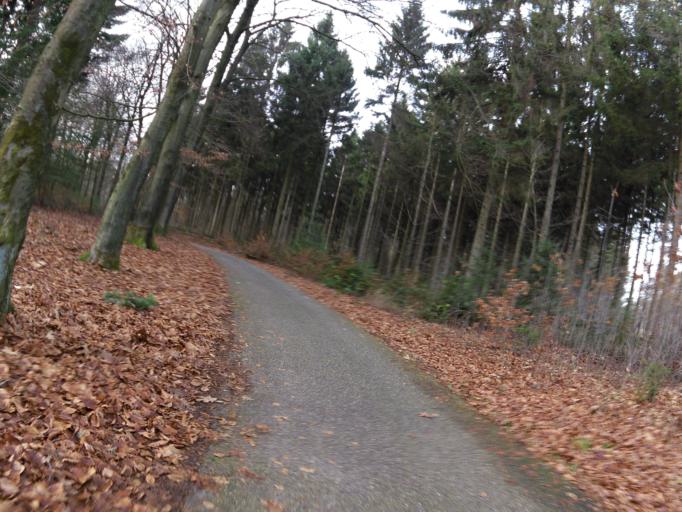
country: NL
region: North Brabant
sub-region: Gemeente Uden
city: Uden
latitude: 51.6928
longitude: 5.6233
